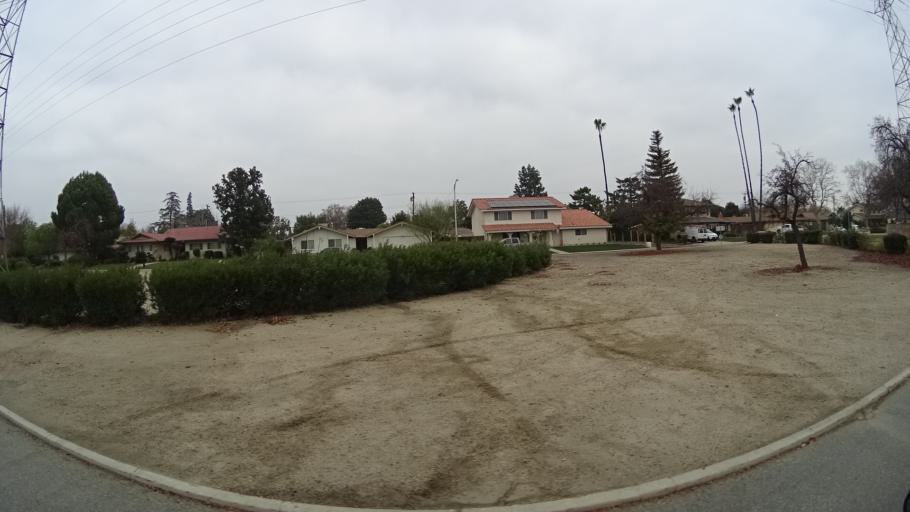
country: US
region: California
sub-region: Kern County
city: Bakersfield
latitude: 35.3868
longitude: -119.0334
